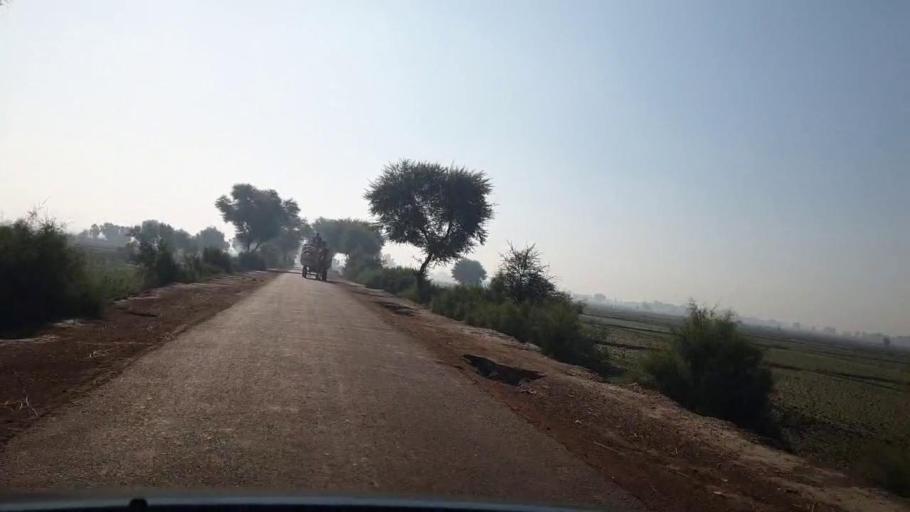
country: PK
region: Sindh
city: Dadu
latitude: 26.6671
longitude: 67.8164
